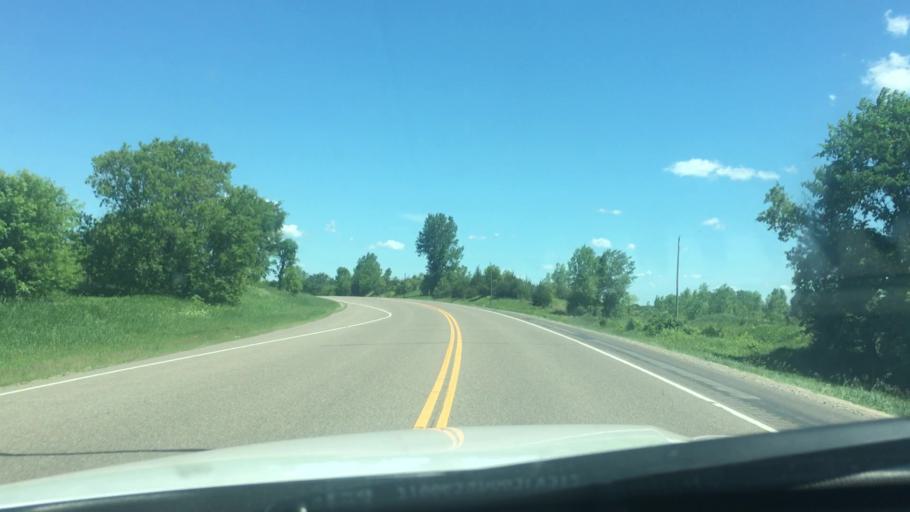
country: US
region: Wisconsin
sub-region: Polk County
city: Osceola
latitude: 45.3498
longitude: -92.7133
